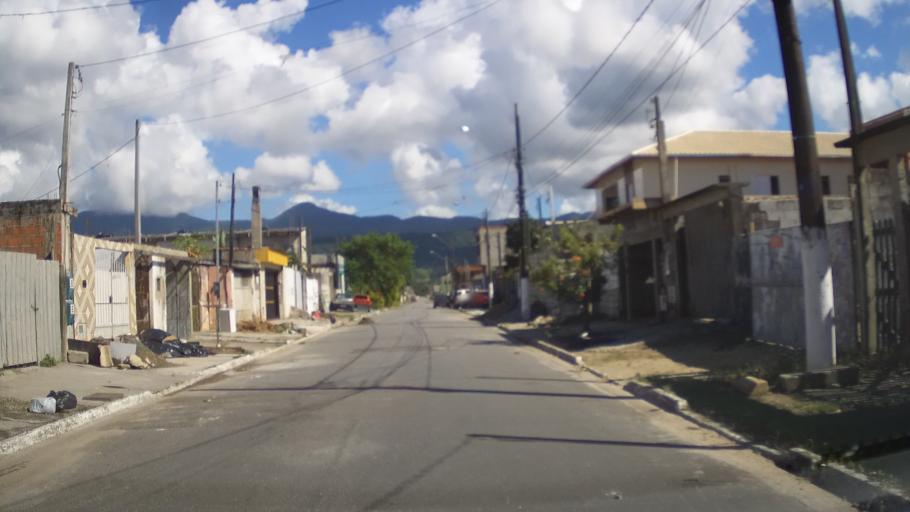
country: BR
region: Sao Paulo
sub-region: Praia Grande
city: Praia Grande
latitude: -24.0212
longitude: -46.5098
